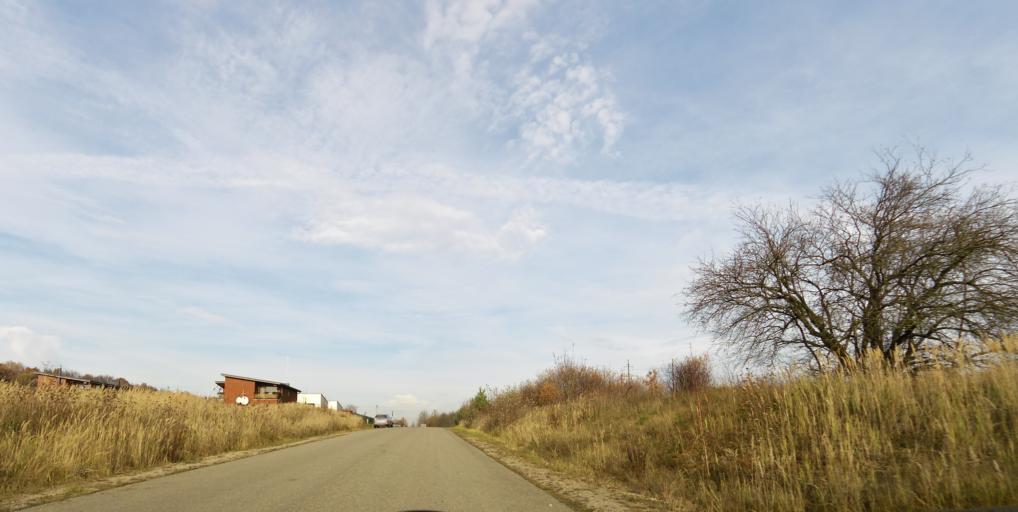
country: LT
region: Vilnius County
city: Justiniskes
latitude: 54.7124
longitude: 25.2061
